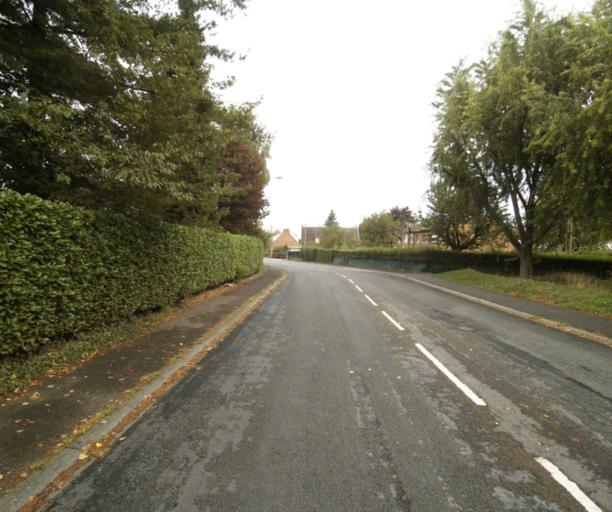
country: FR
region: Nord-Pas-de-Calais
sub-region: Departement du Nord
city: Ronchin
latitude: 50.5942
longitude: 3.0888
